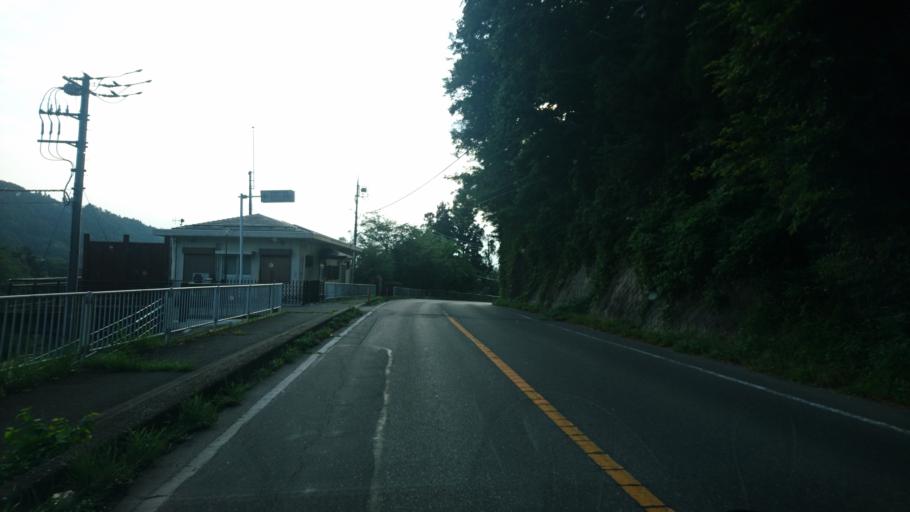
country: JP
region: Gunma
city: Numata
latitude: 36.6597
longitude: 139.1173
